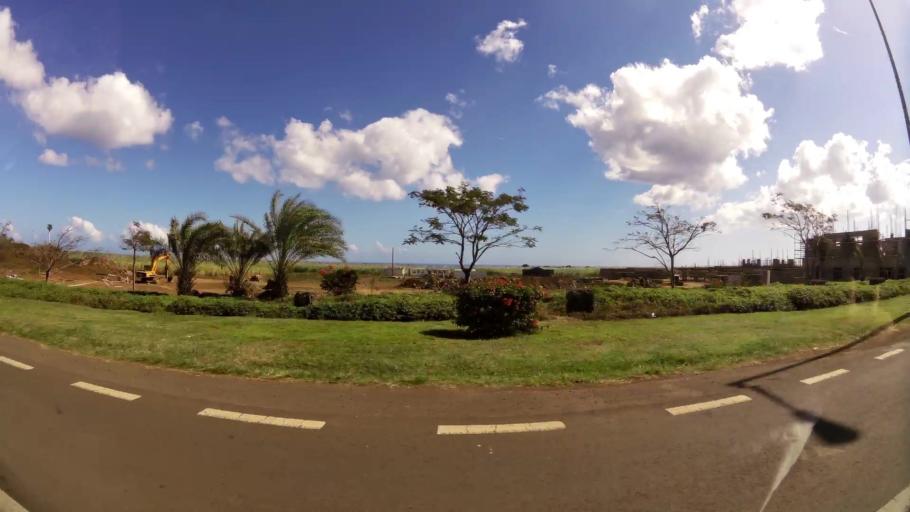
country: MU
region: Black River
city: Cascavelle
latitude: -20.2749
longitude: 57.4052
